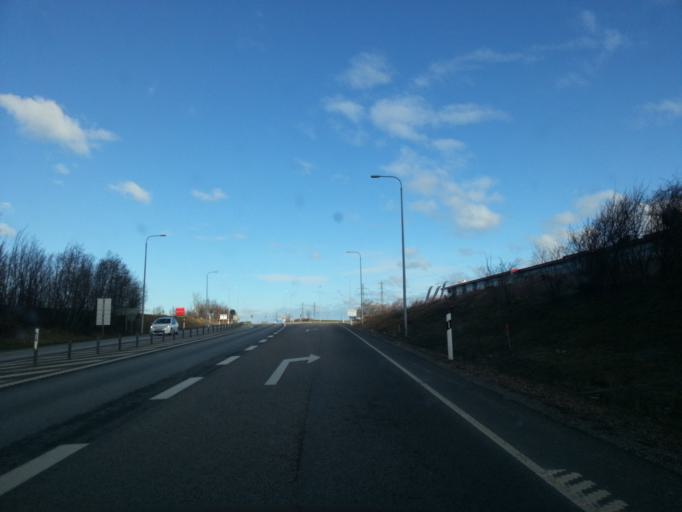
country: SE
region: Skane
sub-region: Lunds Kommun
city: Lund
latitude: 55.7207
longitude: 13.1509
